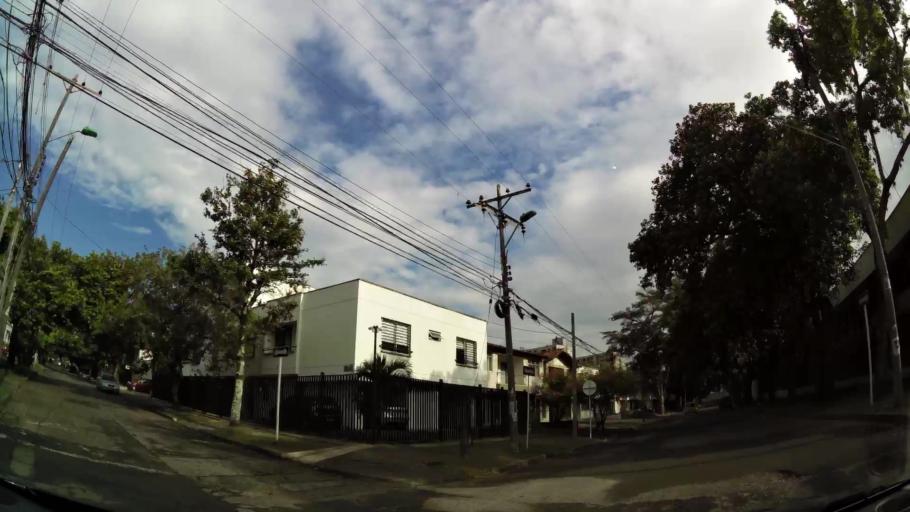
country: CO
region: Valle del Cauca
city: Cali
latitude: 3.4870
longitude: -76.5224
